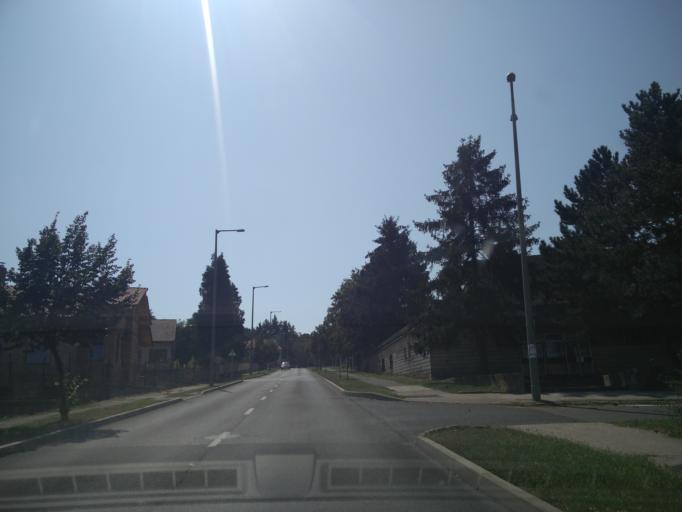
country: HU
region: Zala
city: Zalaegerszeg
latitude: 46.8317
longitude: 16.8375
